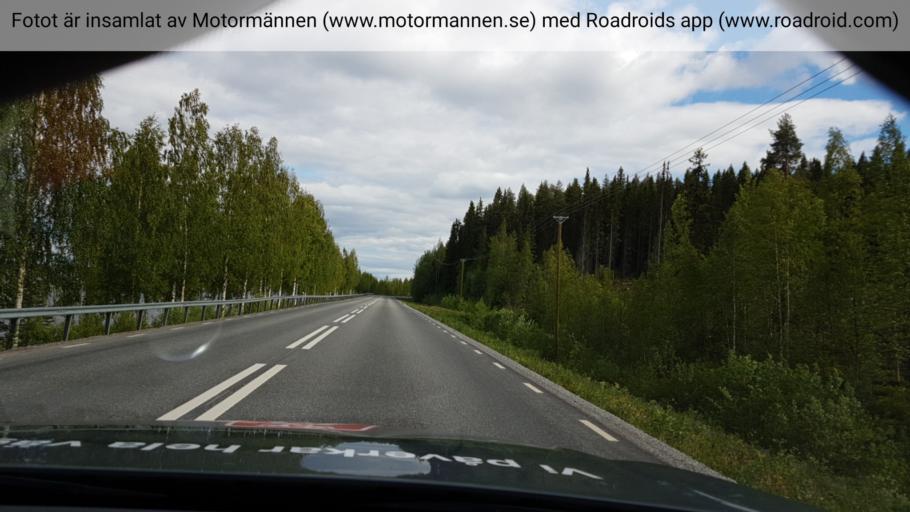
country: SE
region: Jaemtland
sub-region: Stroemsunds Kommun
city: Stroemsund
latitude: 64.1845
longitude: 15.6477
